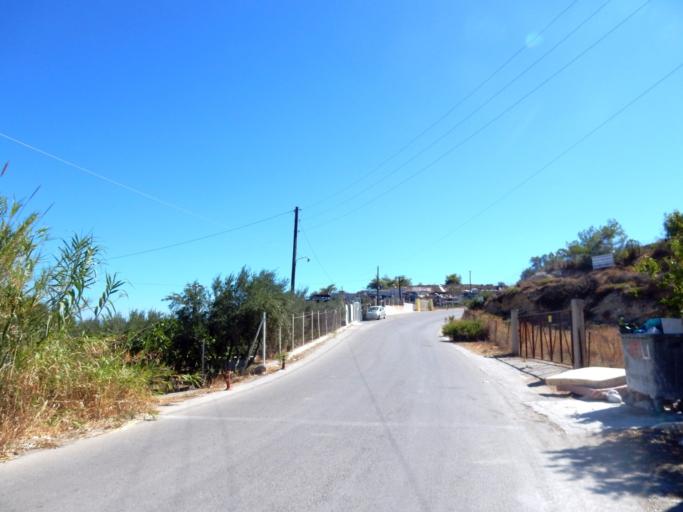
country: GR
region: Attica
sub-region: Nomos Piraios
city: Vathi
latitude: 37.7695
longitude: 23.4714
